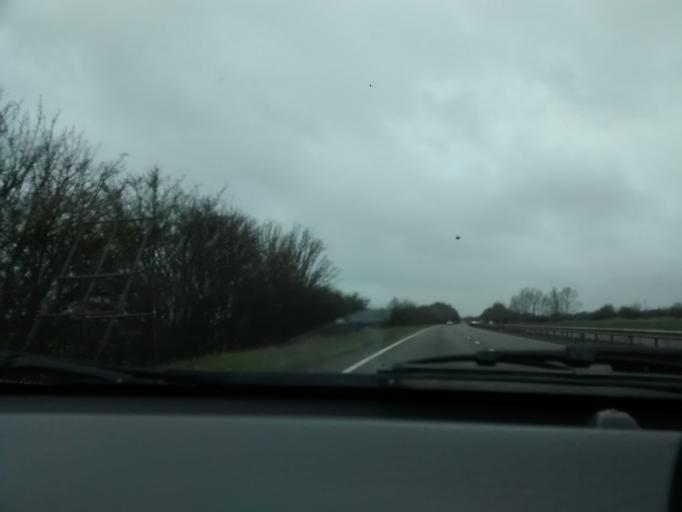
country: GB
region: England
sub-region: Suffolk
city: Needham Market
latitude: 52.1641
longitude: 1.0577
